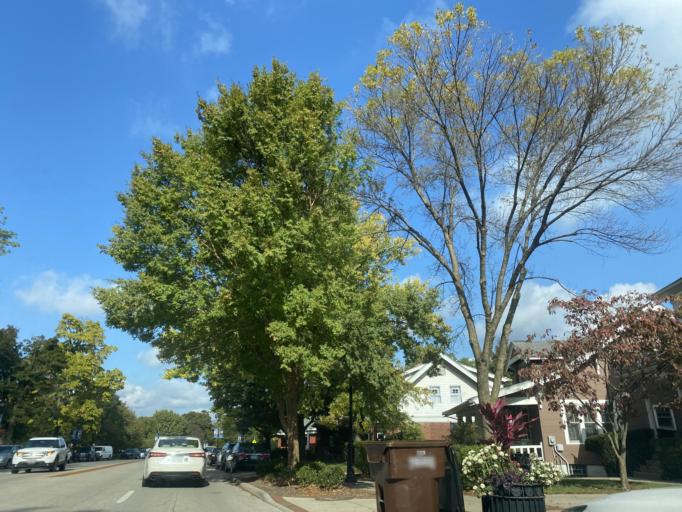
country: US
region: Kentucky
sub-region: Campbell County
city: Fort Thomas
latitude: 39.0816
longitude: -84.4499
